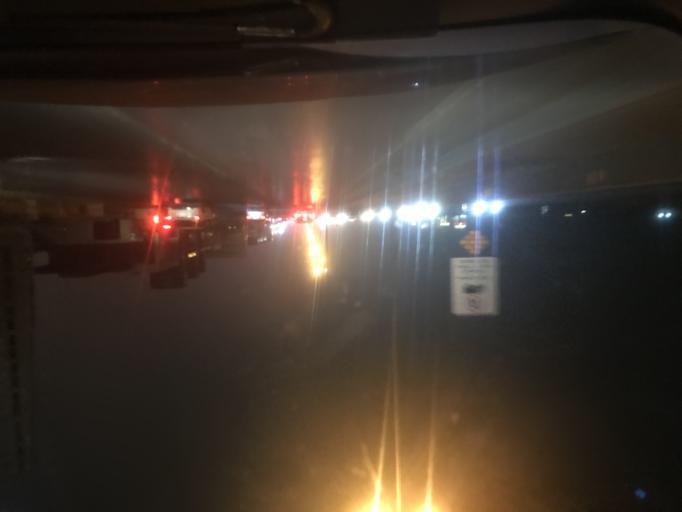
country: SA
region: Ar Riyad
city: Riyadh
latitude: 24.8350
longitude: 46.7373
